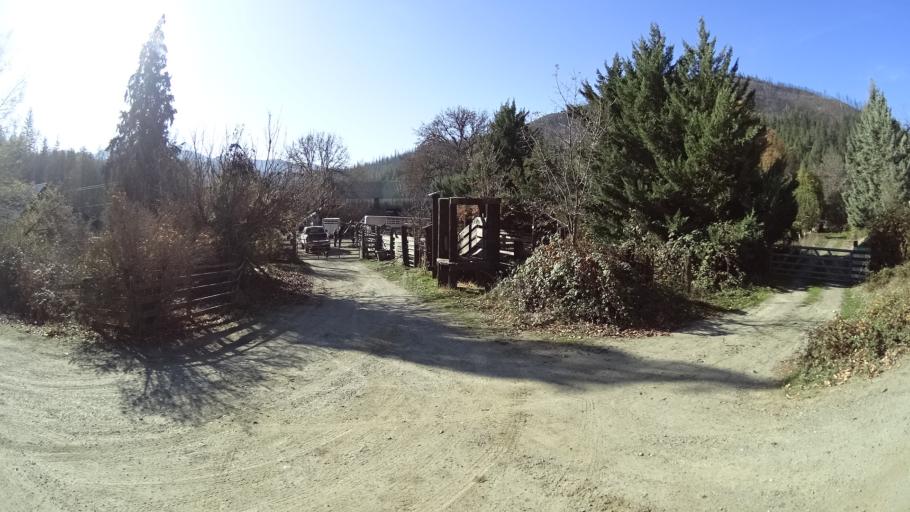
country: US
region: California
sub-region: Siskiyou County
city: Happy Camp
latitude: 41.8379
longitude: -123.0079
